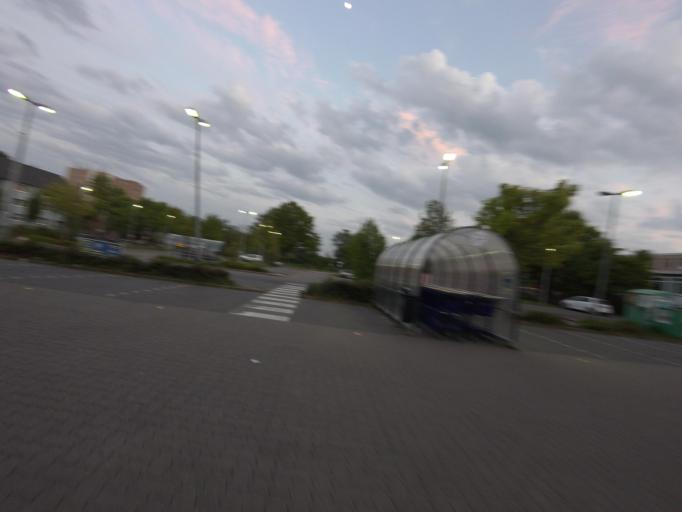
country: DE
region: Lower Saxony
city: Hildesheim
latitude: 52.1460
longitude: 9.9208
